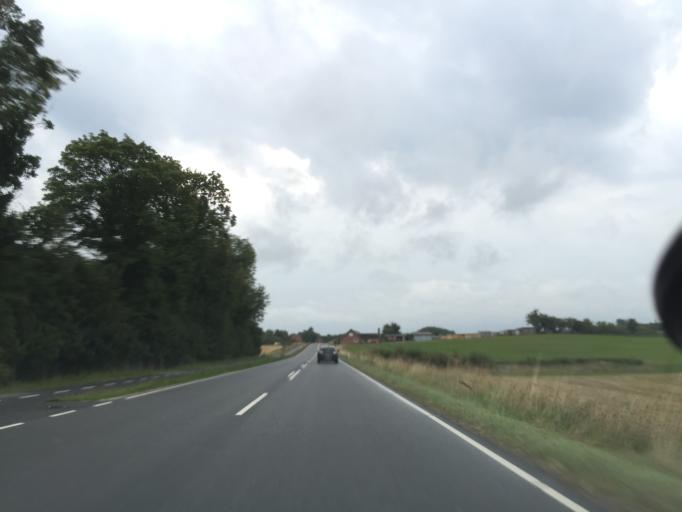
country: DK
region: Central Jutland
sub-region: Skanderborg Kommune
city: Skanderborg
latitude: 56.0960
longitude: 9.8974
